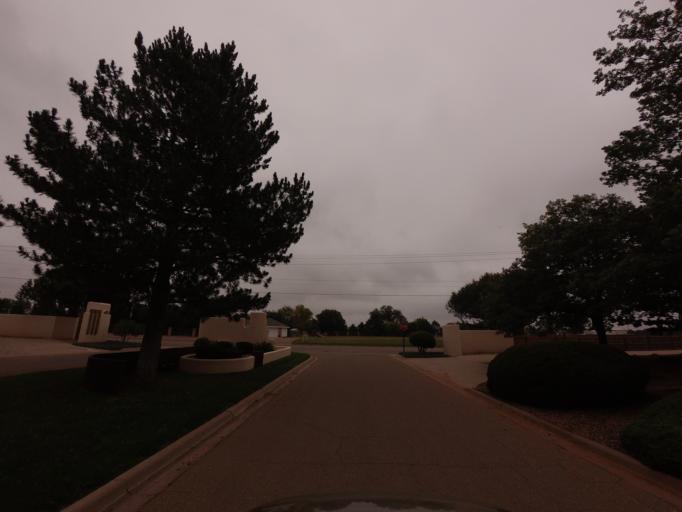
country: US
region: New Mexico
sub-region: Curry County
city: Clovis
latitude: 34.4284
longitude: -103.1789
